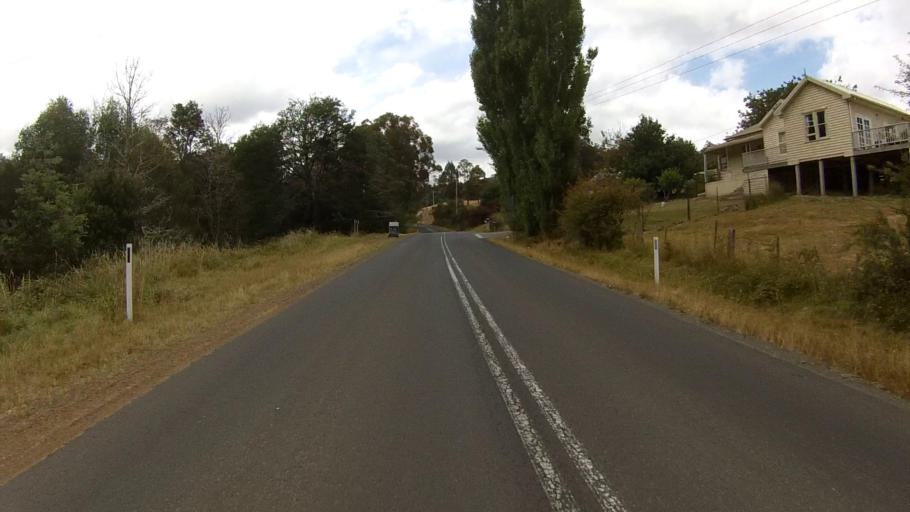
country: AU
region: Tasmania
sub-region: Huon Valley
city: Cygnet
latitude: -43.1488
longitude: 147.1521
